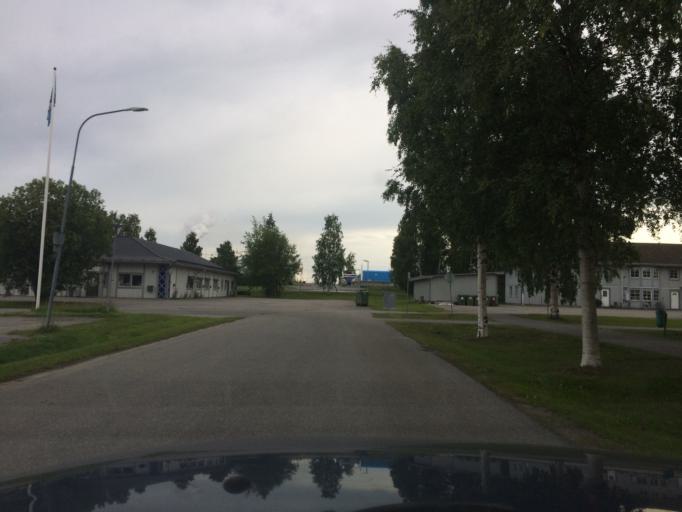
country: SE
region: Norrbotten
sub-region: Pitea Kommun
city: Pitea
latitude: 65.3257
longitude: 21.4436
